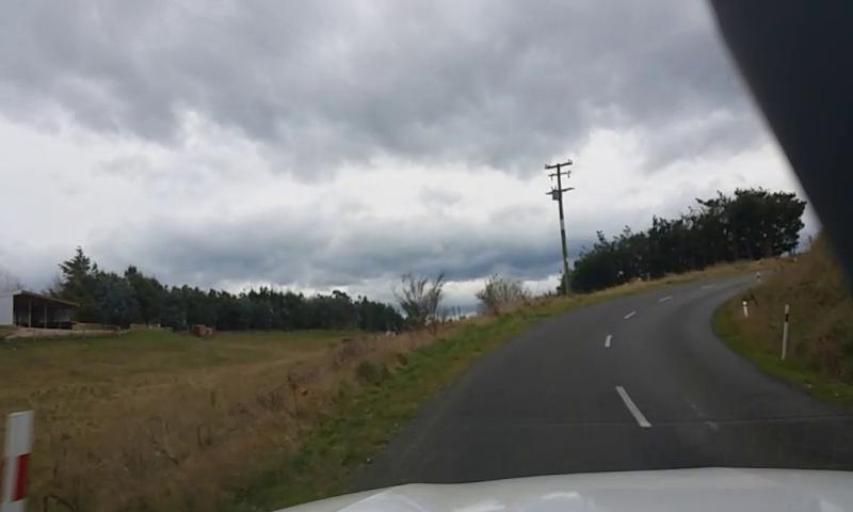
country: NZ
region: Canterbury
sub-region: Waimakariri District
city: Kaiapoi
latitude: -43.2971
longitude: 172.4376
